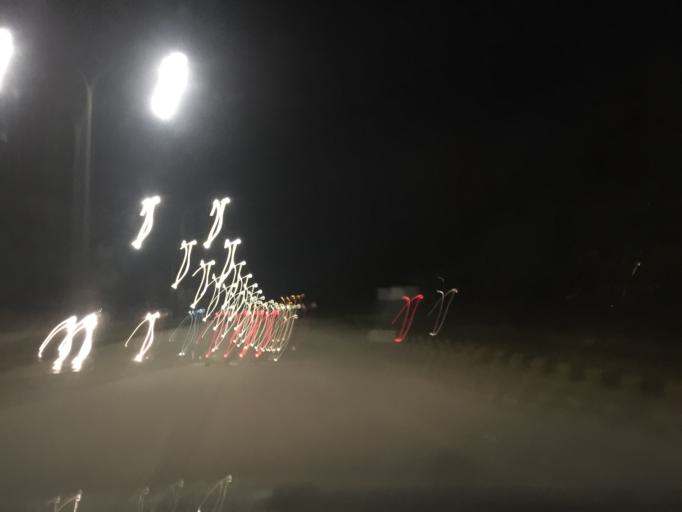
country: JO
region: Amman
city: Umm as Summaq
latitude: 31.8758
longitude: 35.8396
